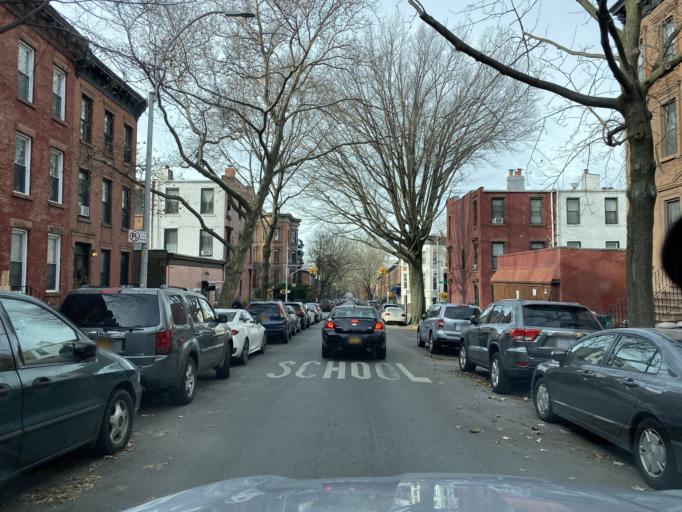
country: US
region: New York
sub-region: Kings County
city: Brooklyn
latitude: 40.6695
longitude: -73.9818
